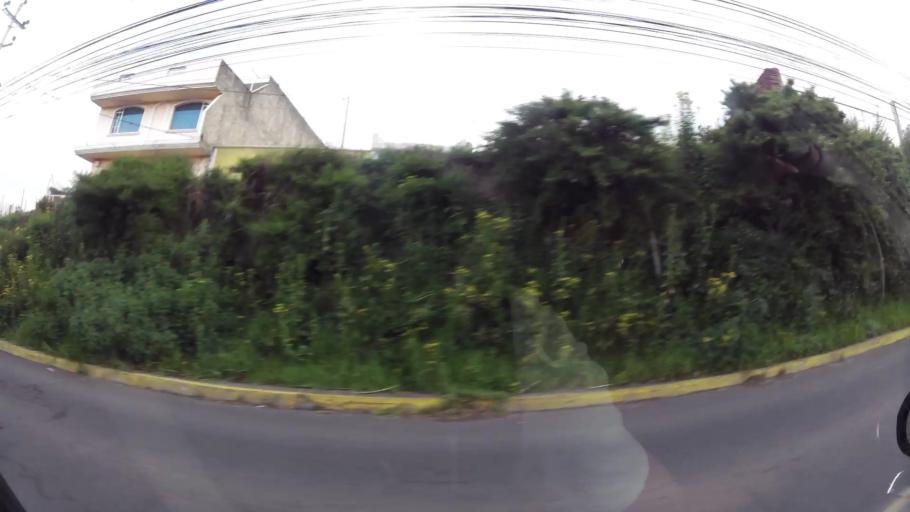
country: EC
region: Pichincha
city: Sangolqui
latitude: -0.2904
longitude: -78.4887
